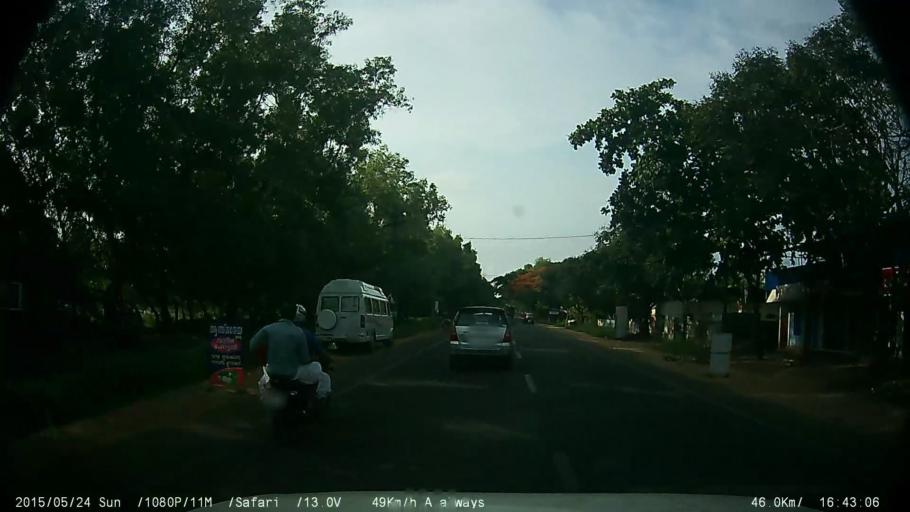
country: IN
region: Kerala
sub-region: Alappuzha
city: Shertallai
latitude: 9.6461
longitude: 76.3360
